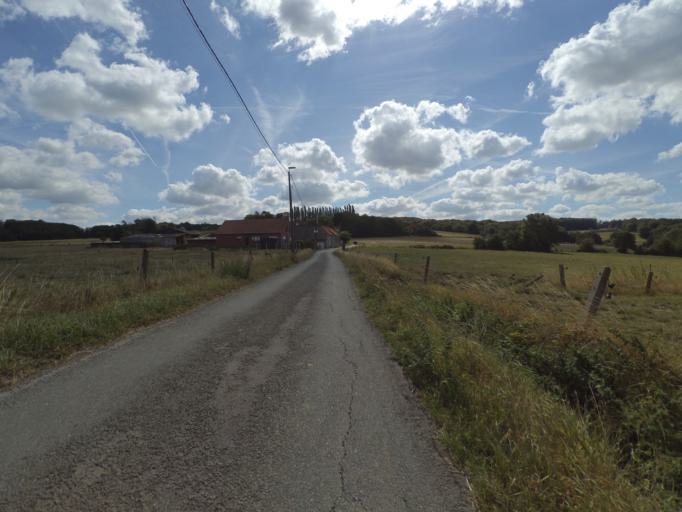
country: BE
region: Wallonia
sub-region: Province du Hainaut
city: Frasnes-lez-Anvaing
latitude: 50.7255
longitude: 3.6289
